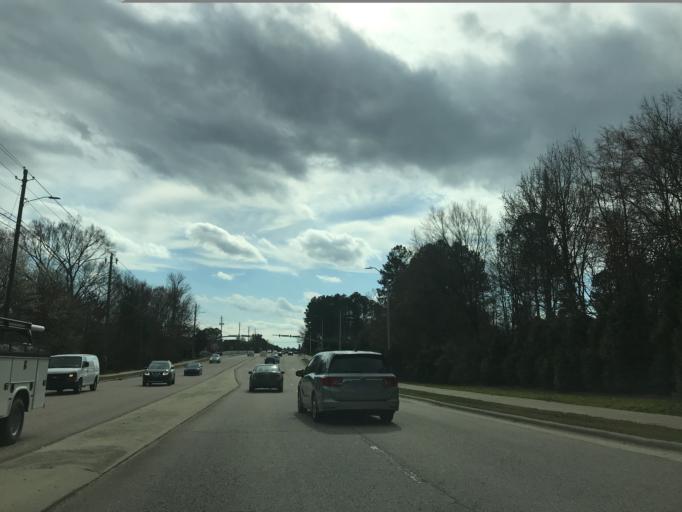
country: US
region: North Carolina
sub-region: Wake County
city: Morrisville
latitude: 35.8050
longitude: -78.8487
